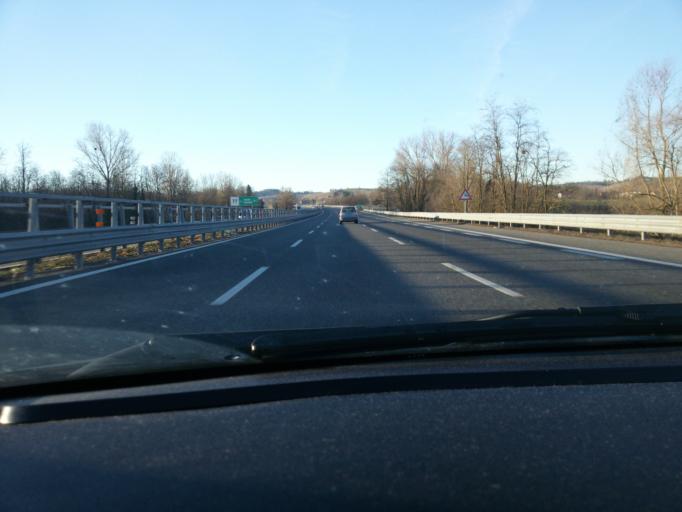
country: IT
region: Piedmont
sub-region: Provincia di Alessandria
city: Mirabello Monferrato
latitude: 45.0212
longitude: 8.5366
